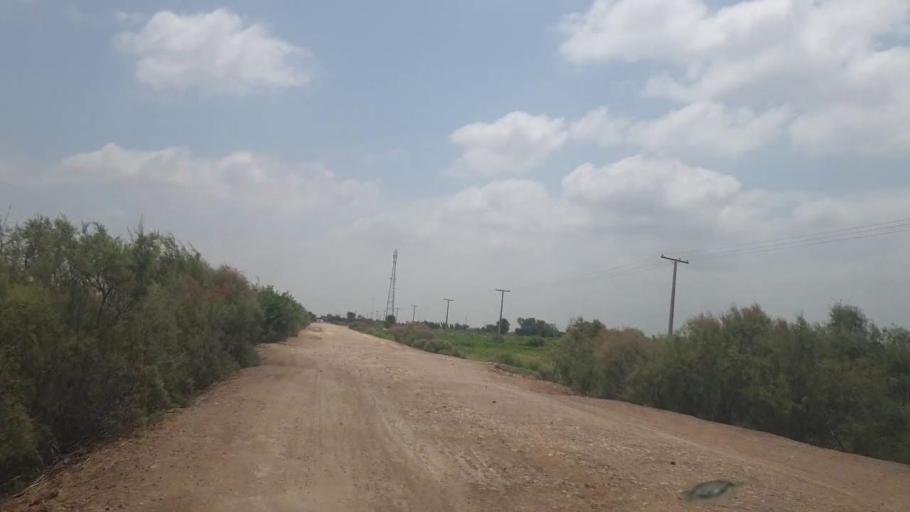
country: PK
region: Sindh
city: Tando Mittha Khan
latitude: 25.9174
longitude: 69.2204
